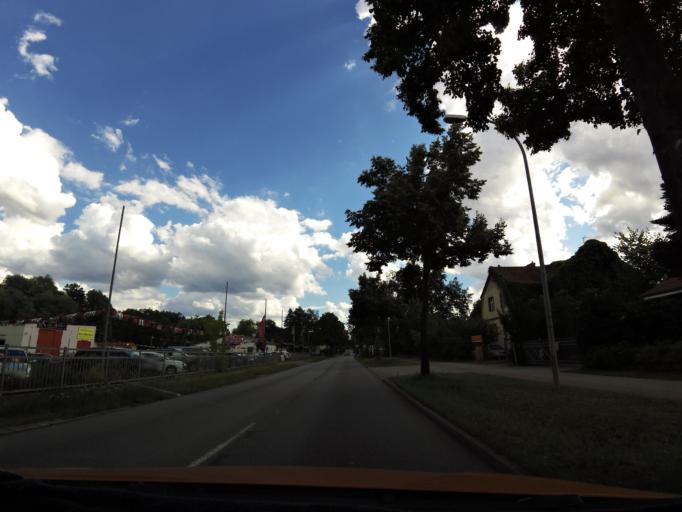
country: DE
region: Brandenburg
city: Konigs Wusterhausen
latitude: 52.3090
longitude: 13.6330
